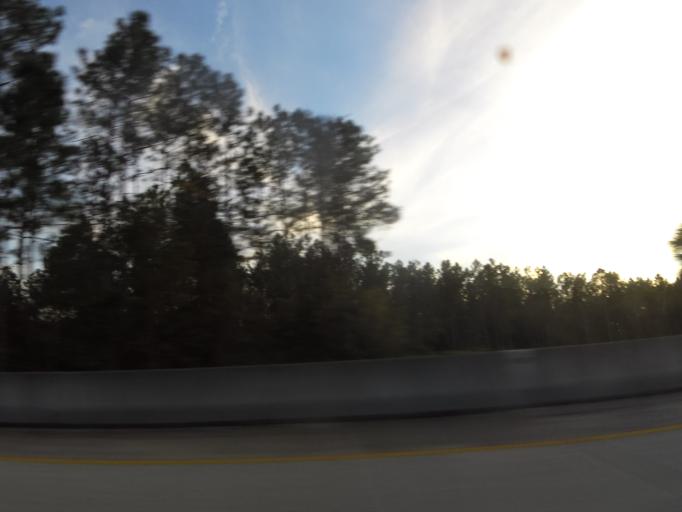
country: US
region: Florida
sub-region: Saint Johns County
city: Palm Valley
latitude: 30.1027
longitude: -81.4702
